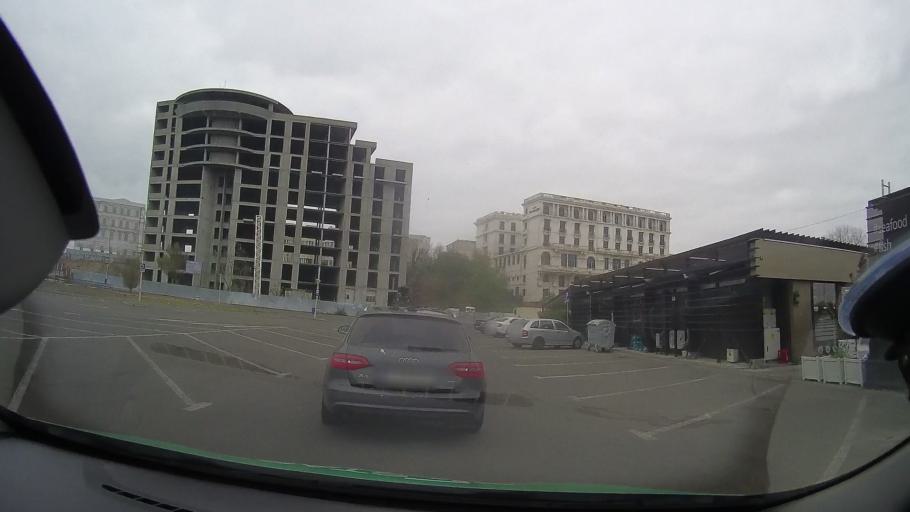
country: RO
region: Constanta
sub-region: Municipiul Constanta
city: Constanta
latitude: 44.1742
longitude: 28.6637
